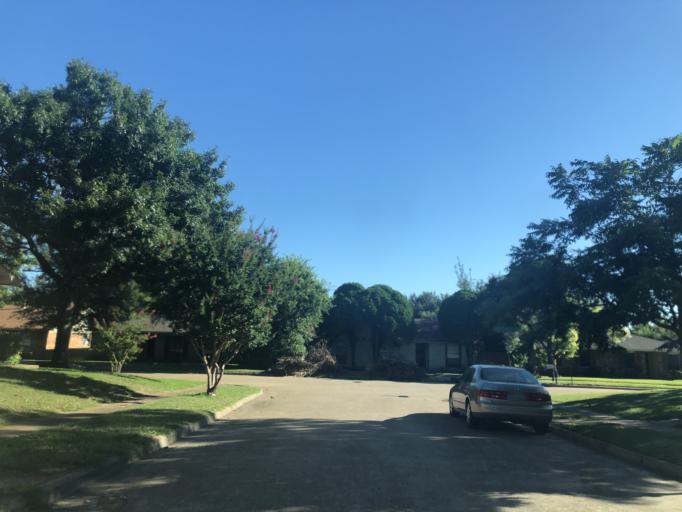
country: US
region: Texas
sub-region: Dallas County
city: Duncanville
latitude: 32.6381
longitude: -96.9512
